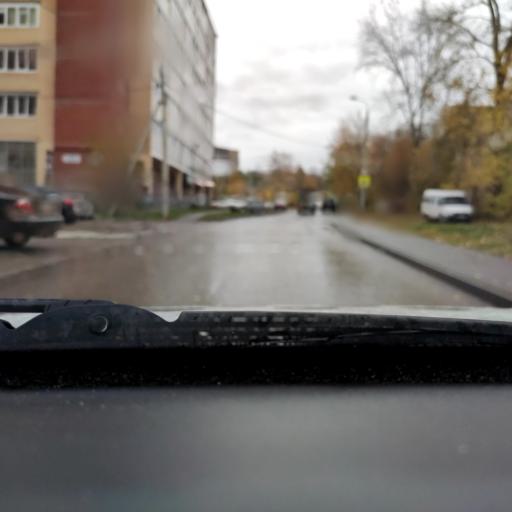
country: RU
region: Perm
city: Perm
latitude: 57.9888
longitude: 56.2230
